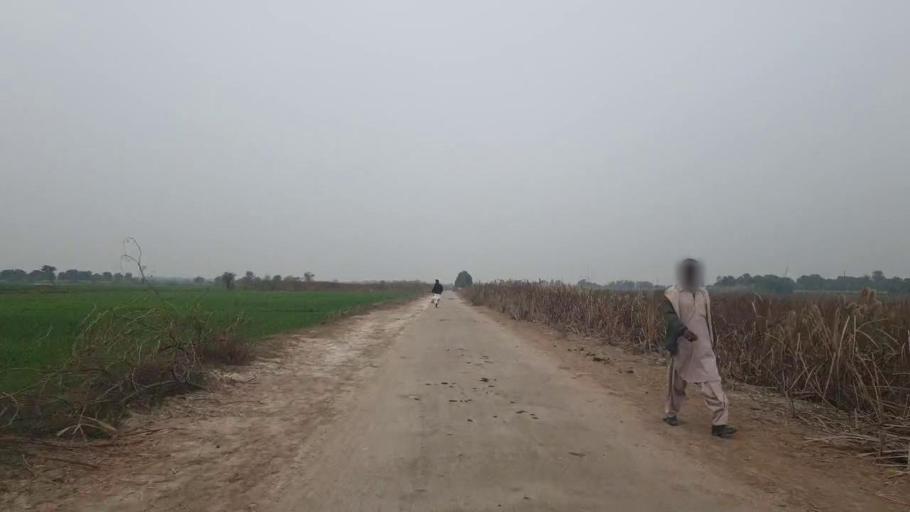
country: PK
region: Sindh
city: Tando Adam
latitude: 25.8376
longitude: 68.6575
